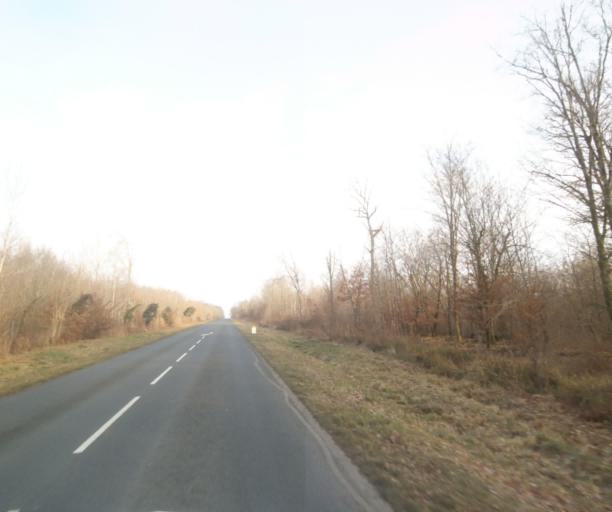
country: FR
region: Champagne-Ardenne
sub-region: Departement de la Haute-Marne
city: Bettancourt-la-Ferree
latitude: 48.6840
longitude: 4.9429
